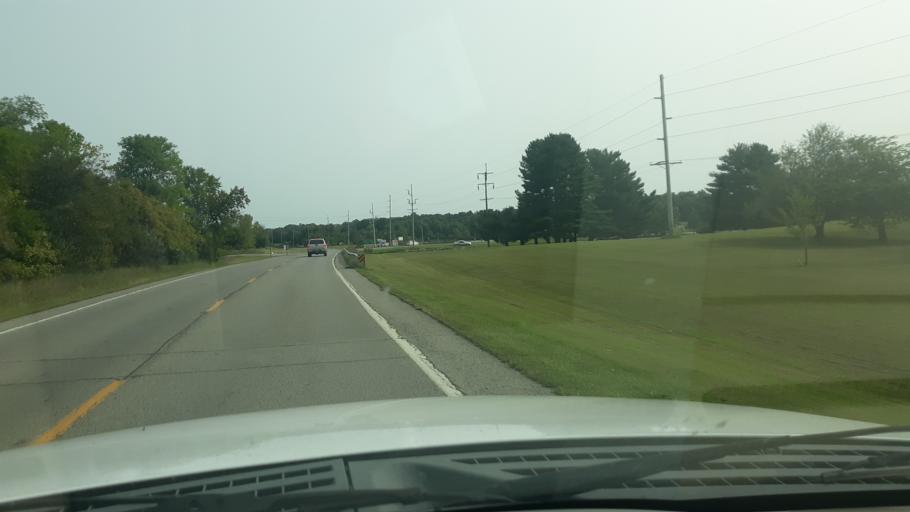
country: US
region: Illinois
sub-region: White County
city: Norris City
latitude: 37.9792
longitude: -88.3166
